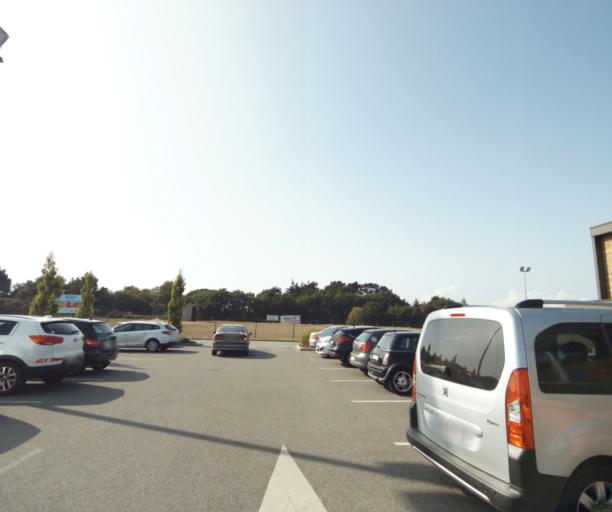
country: FR
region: Brittany
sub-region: Departement du Morbihan
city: Riantec
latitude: 47.7272
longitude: -3.3204
